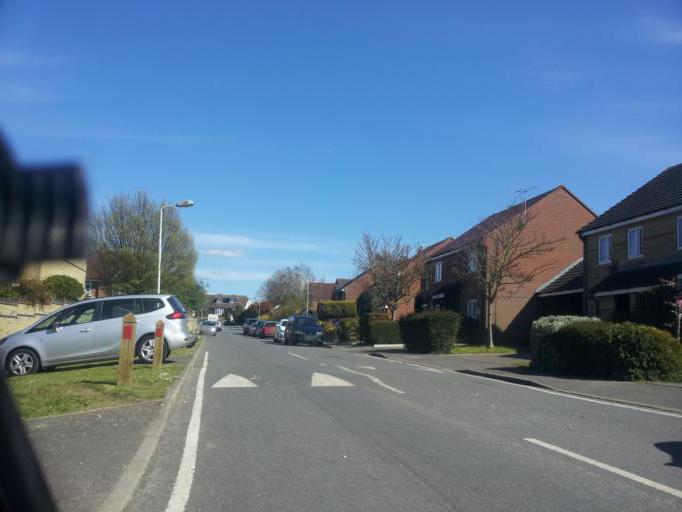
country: GB
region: England
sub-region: Kent
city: Newington
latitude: 51.3498
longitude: 0.6622
